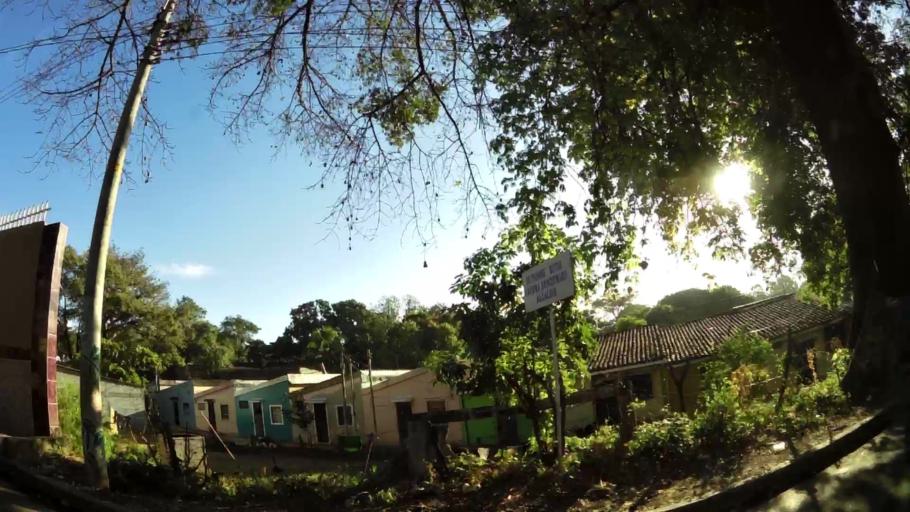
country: SV
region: Sonsonate
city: Sonsonate
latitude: 13.7256
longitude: -89.7307
